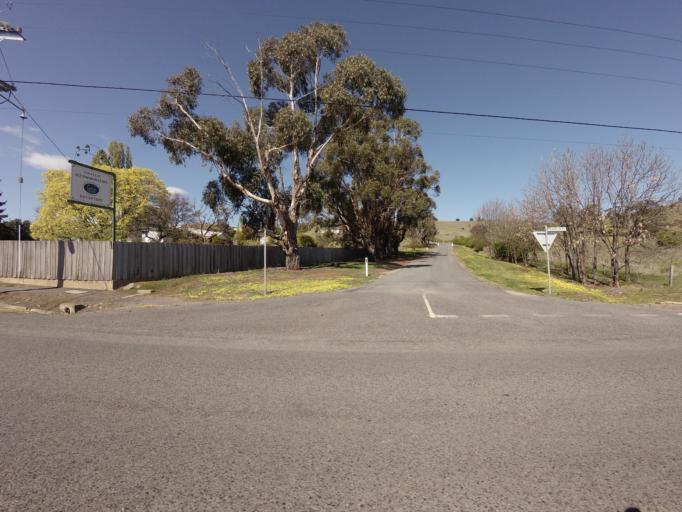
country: AU
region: Tasmania
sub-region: Derwent Valley
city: New Norfolk
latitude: -42.5569
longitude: 146.8337
